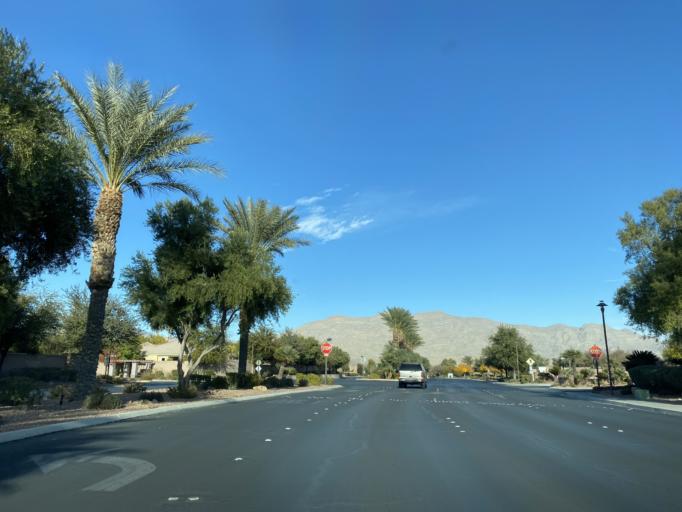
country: US
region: Nevada
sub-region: Clark County
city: North Las Vegas
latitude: 36.3120
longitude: -115.2600
